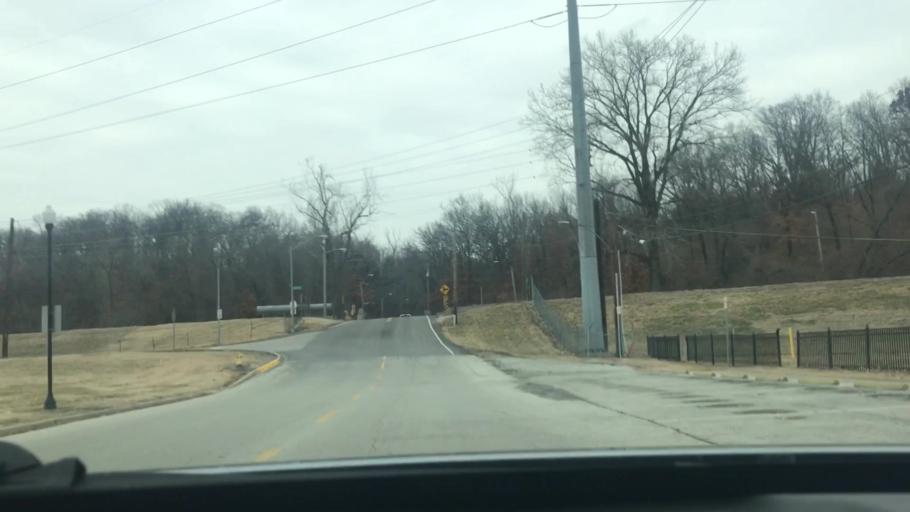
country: US
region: Missouri
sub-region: Clay County
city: North Kansas City
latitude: 39.1514
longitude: -94.5726
